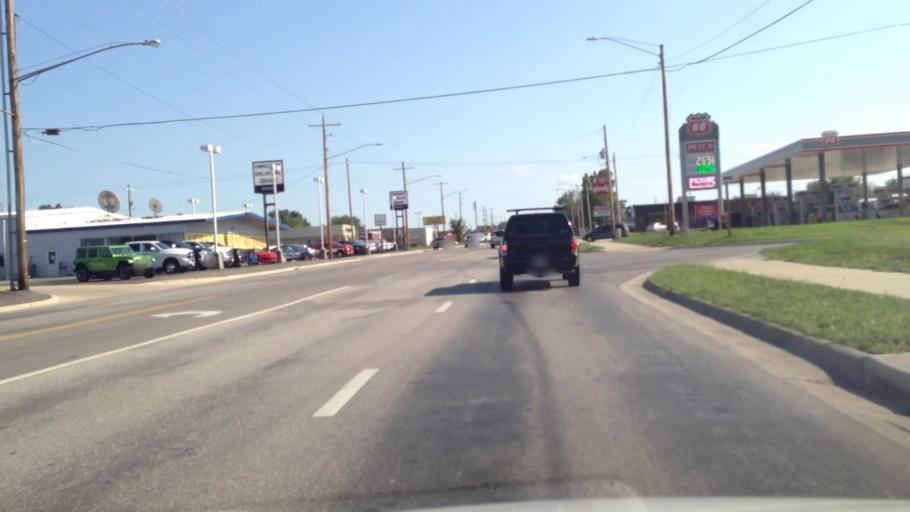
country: US
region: Kansas
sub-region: Bourbon County
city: Fort Scott
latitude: 37.8179
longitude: -94.7056
